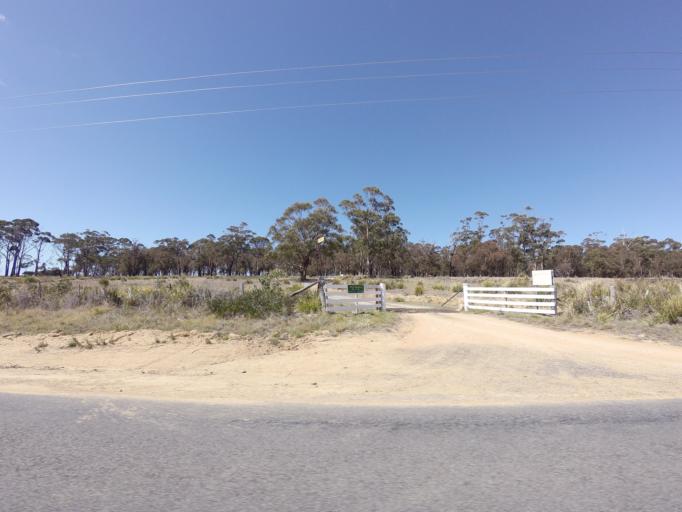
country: AU
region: Tasmania
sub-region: Break O'Day
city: St Helens
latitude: -41.6925
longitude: 148.2809
